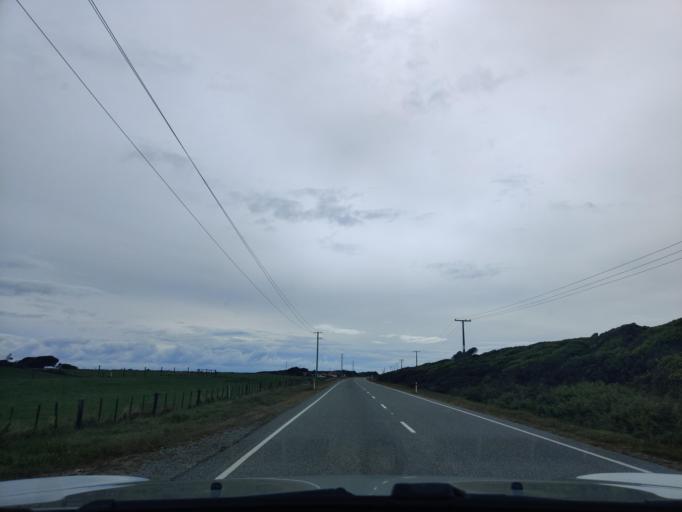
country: NZ
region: West Coast
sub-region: Westland District
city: Hokitika
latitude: -42.7950
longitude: 170.8933
